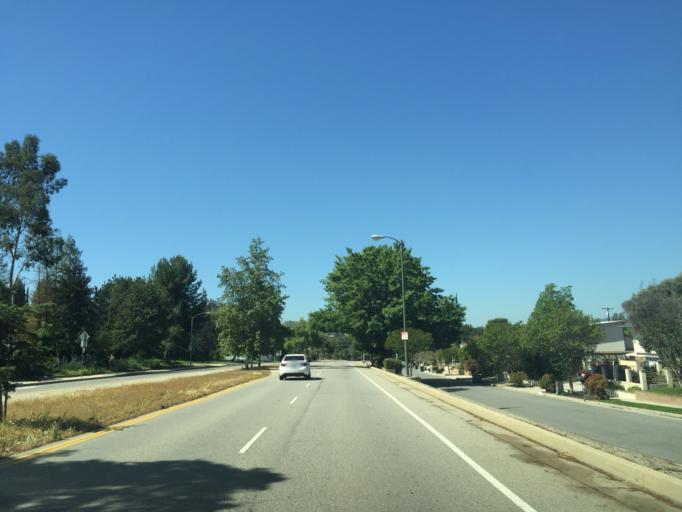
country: US
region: California
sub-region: Los Angeles County
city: Calabasas
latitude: 34.1500
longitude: -118.6187
